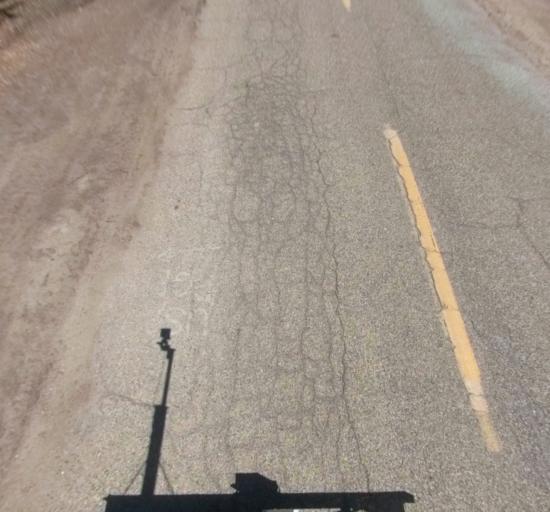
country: US
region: California
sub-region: Madera County
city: Chowchilla
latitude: 37.0716
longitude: -120.3108
